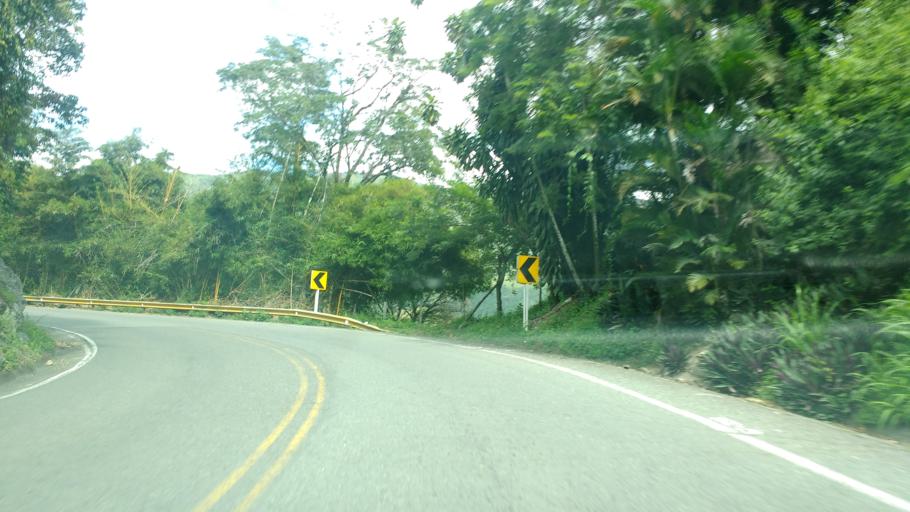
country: CO
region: Antioquia
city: Titiribi
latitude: 6.0223
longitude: -75.7620
